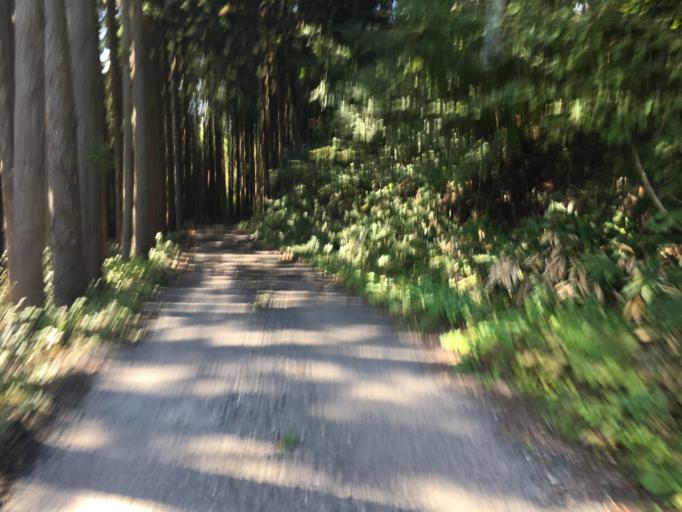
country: JP
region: Yamagata
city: Yonezawa
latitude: 37.8249
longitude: 140.2226
